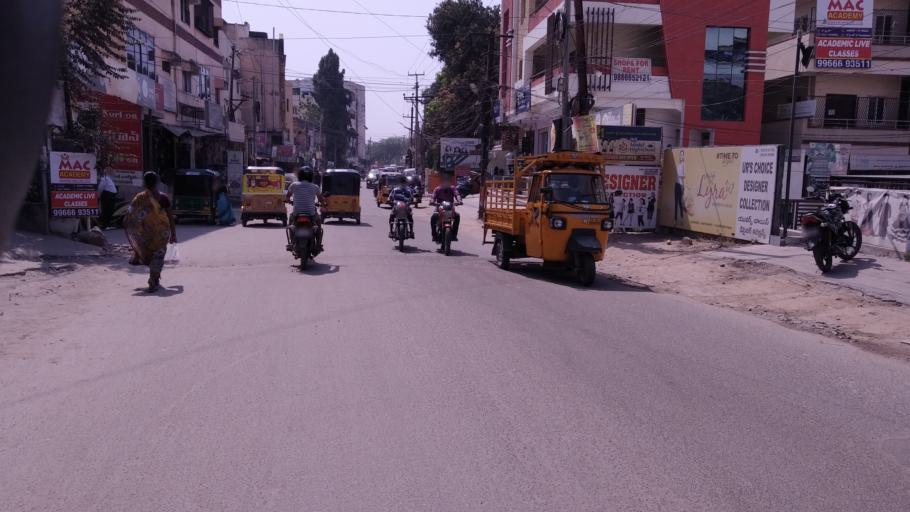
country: IN
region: Telangana
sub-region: Rangareddi
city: Quthbullapur
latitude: 17.4708
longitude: 78.4838
